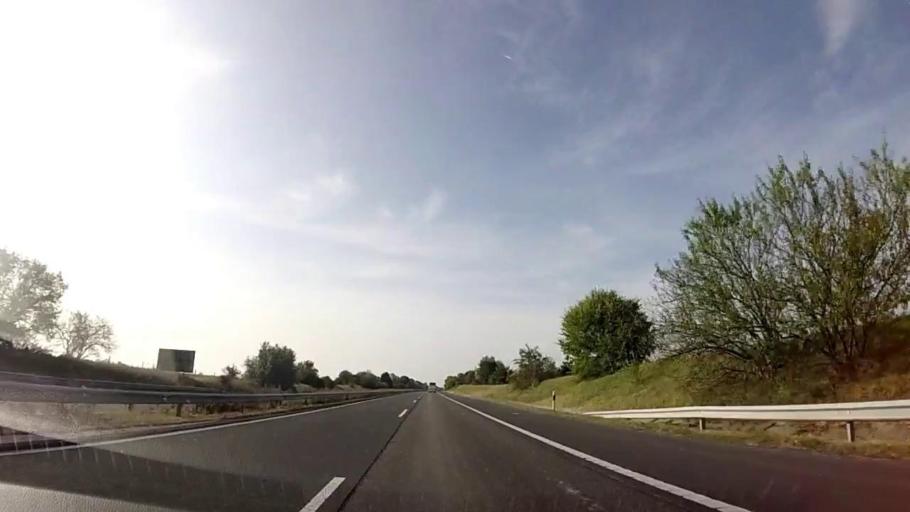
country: HU
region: Fejer
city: Lepseny
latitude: 46.9722
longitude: 18.1694
